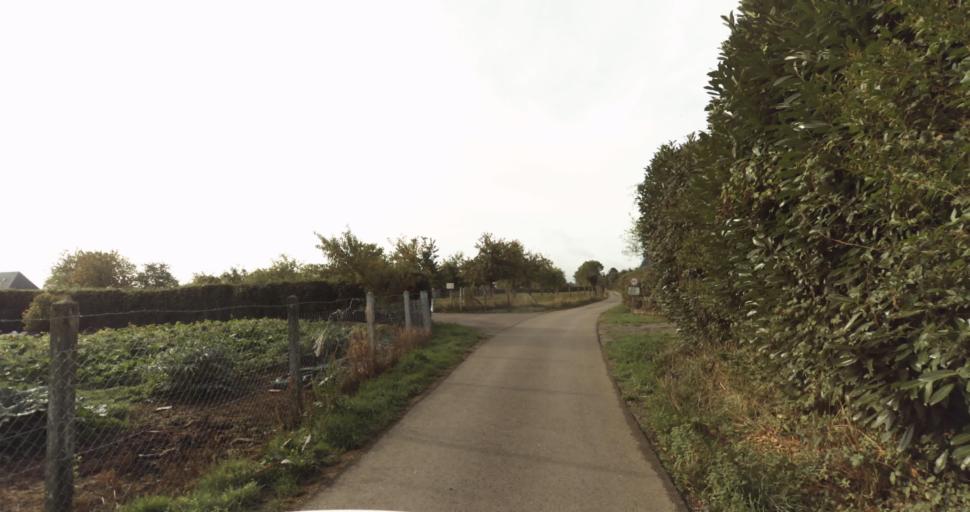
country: FR
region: Lower Normandy
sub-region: Departement de l'Orne
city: Vimoutiers
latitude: 48.9123
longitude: 0.3047
